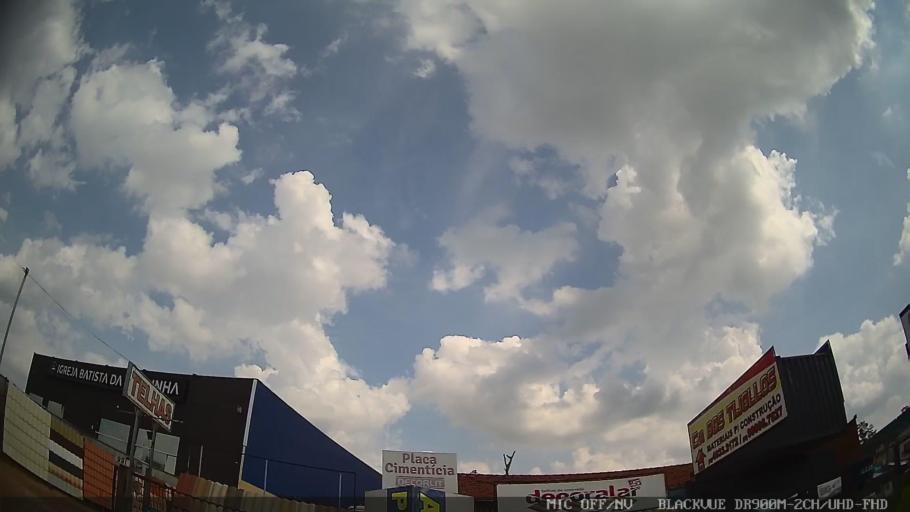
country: BR
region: Sao Paulo
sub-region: Braganca Paulista
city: Braganca Paulista
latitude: -22.9680
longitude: -46.5545
